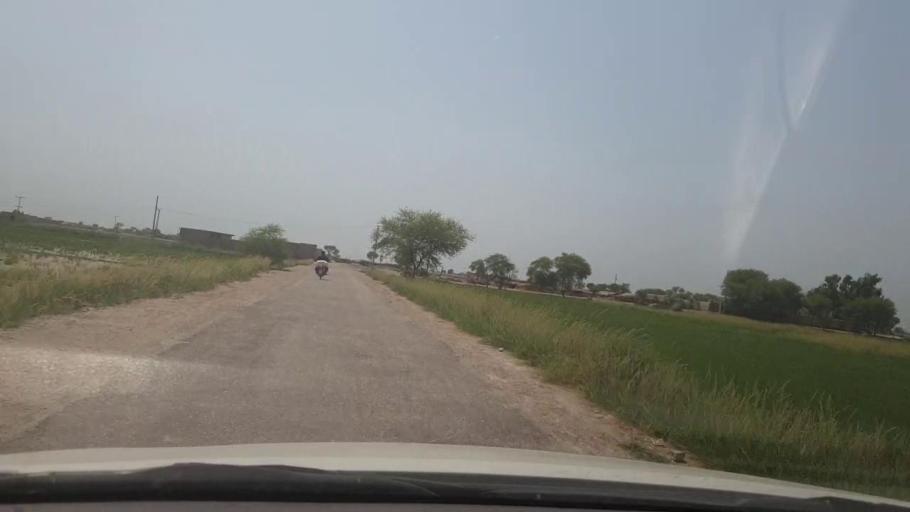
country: PK
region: Sindh
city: Shikarpur
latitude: 27.9935
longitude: 68.5753
